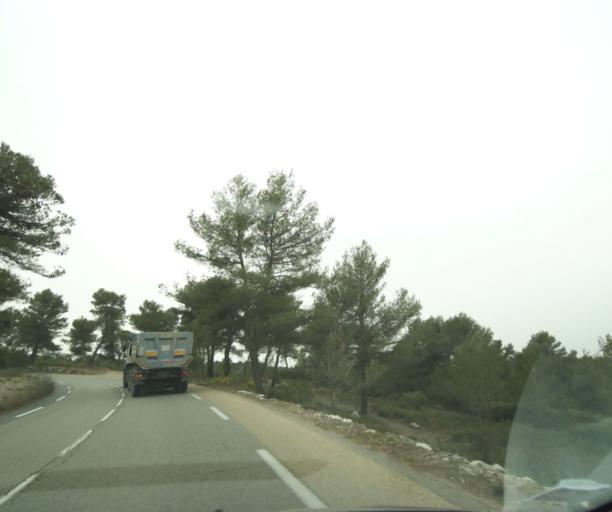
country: FR
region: Provence-Alpes-Cote d'Azur
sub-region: Departement des Bouches-du-Rhone
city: Belcodene
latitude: 43.4240
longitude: 5.6173
